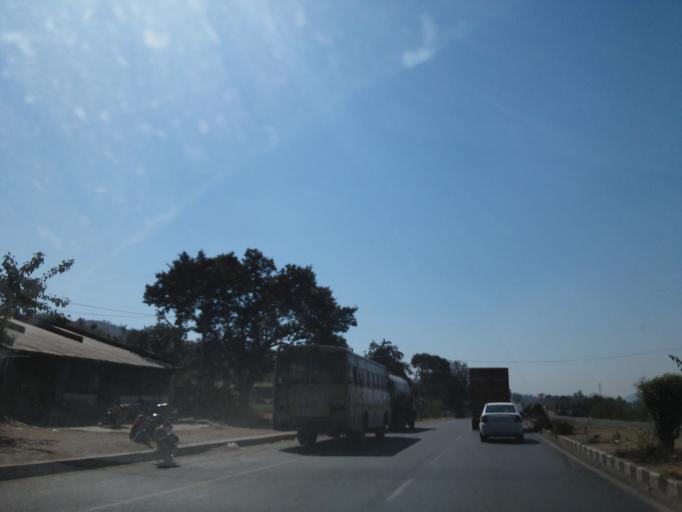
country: IN
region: Gujarat
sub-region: Sabar Kantha
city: Meghraj
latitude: 23.7548
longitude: 73.4405
